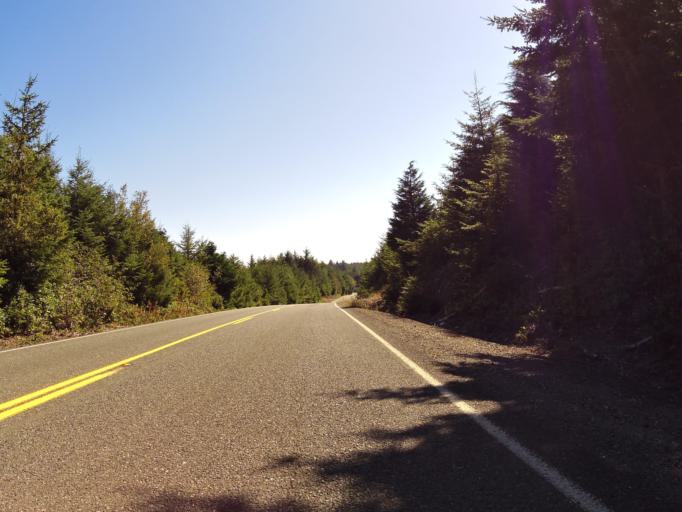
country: US
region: Oregon
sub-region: Coos County
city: Barview
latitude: 43.2699
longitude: -124.3473
